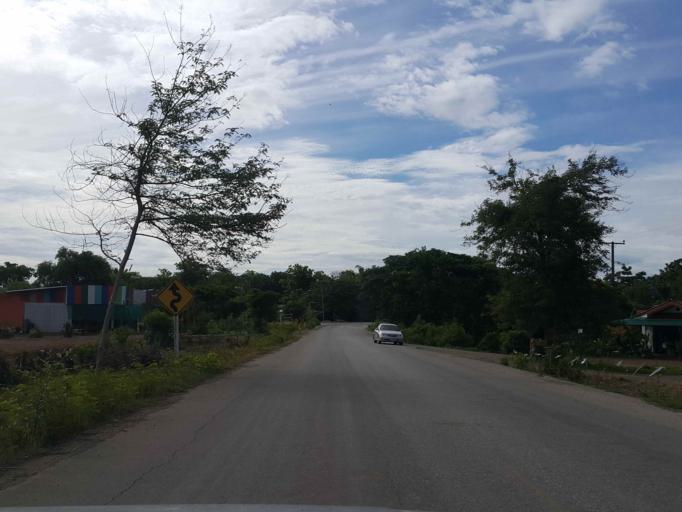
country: TH
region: Sukhothai
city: Thung Saliam
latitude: 17.2702
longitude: 99.5331
